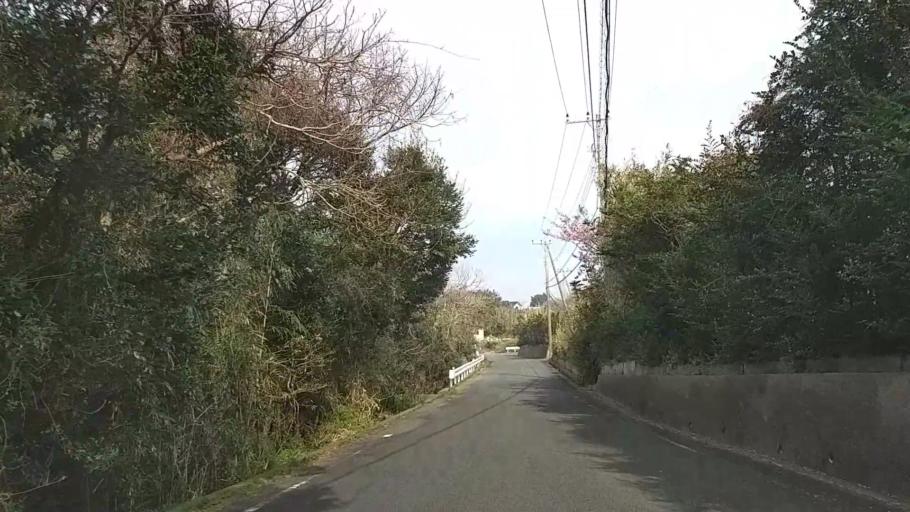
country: JP
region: Shizuoka
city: Shimoda
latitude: 34.6563
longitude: 138.9630
